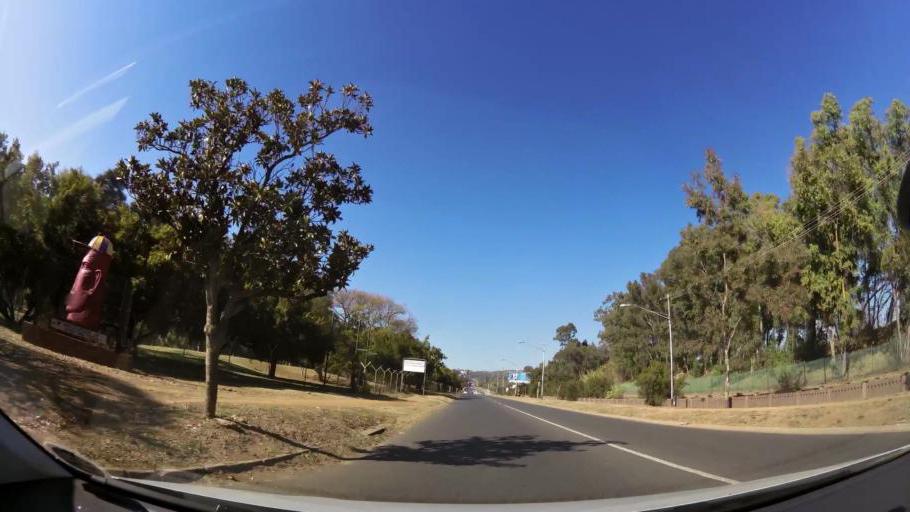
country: ZA
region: Gauteng
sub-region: City of Tshwane Metropolitan Municipality
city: Pretoria
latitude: -25.7681
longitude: 28.2223
